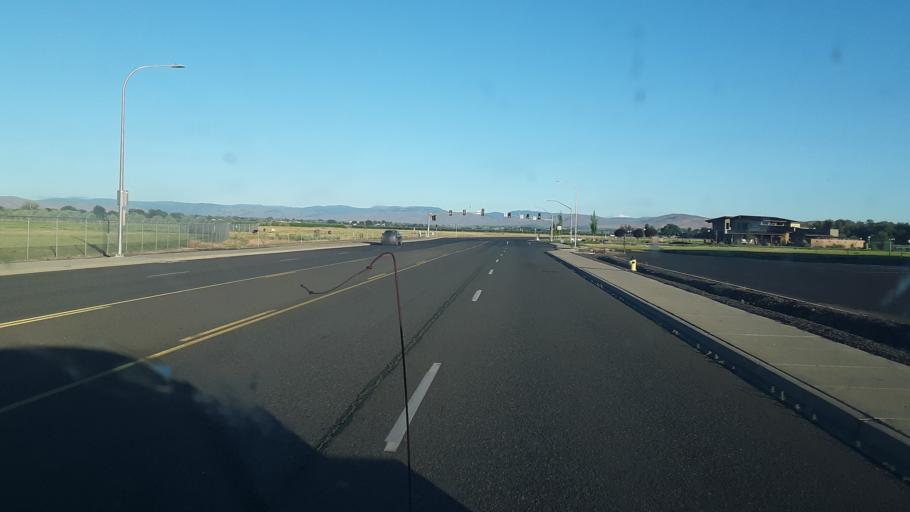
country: US
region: Washington
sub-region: Yakima County
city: West Valley
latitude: 46.5749
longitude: -120.5598
